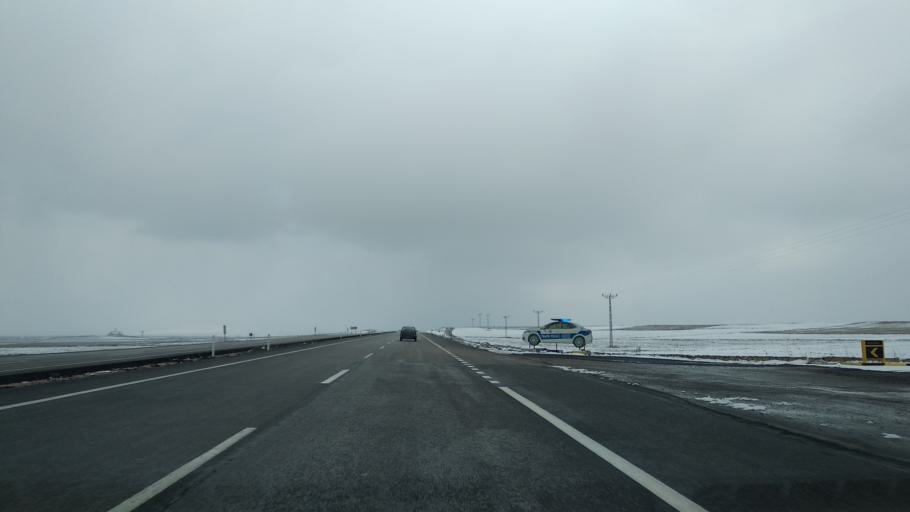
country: TR
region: Kayseri
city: Elbasi
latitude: 38.6523
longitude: 36.0004
